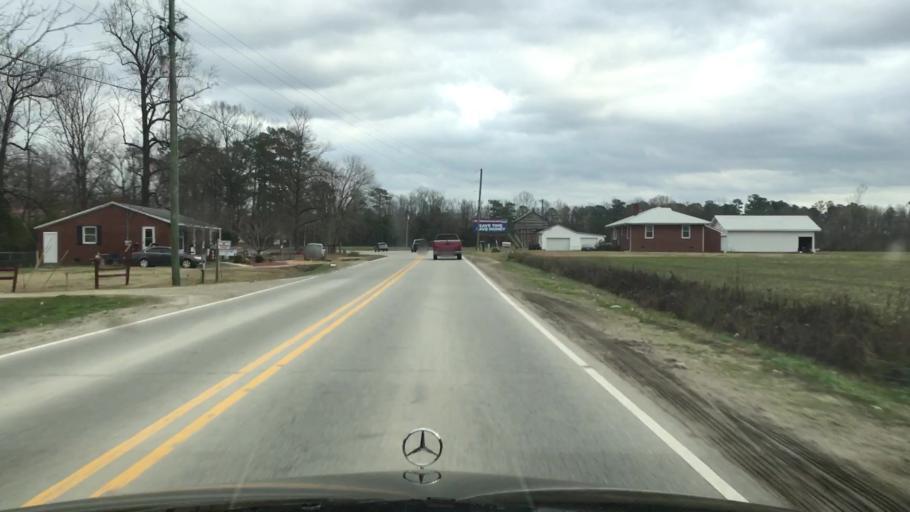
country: US
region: North Carolina
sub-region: Onslow County
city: Richlands
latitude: 34.8788
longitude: -77.5181
